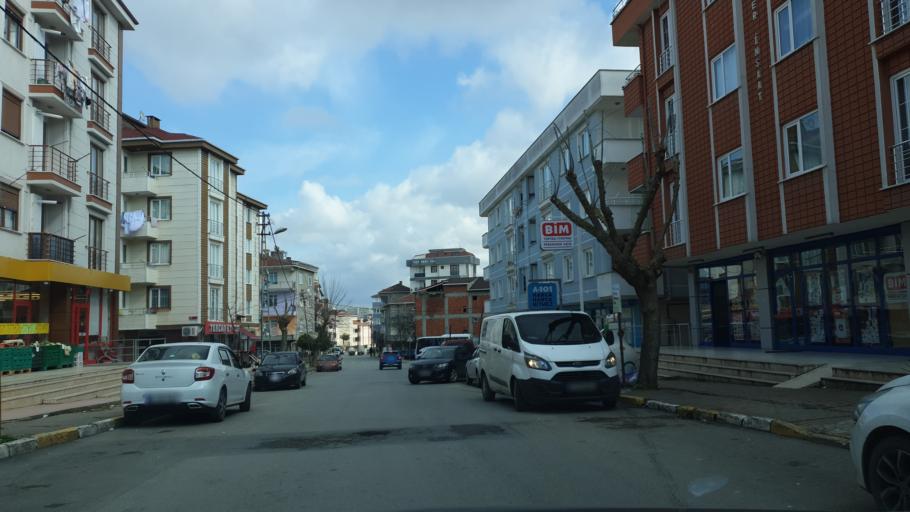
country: TR
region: Istanbul
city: Icmeler
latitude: 40.8666
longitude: 29.3065
